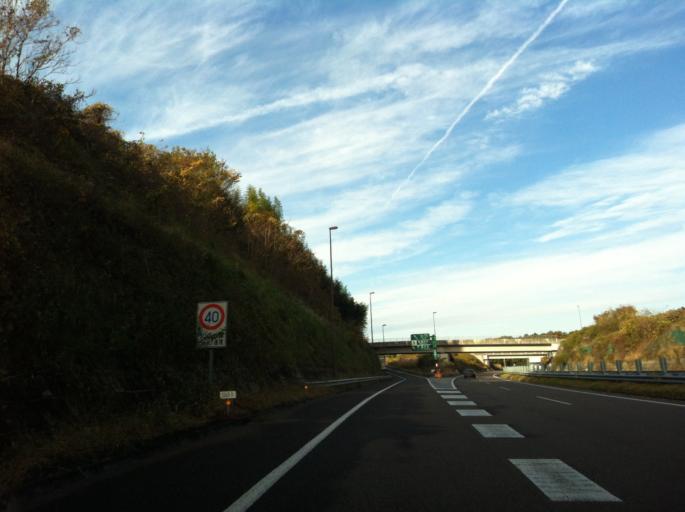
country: JP
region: Gifu
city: Minokamo
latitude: 35.4695
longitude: 137.0250
